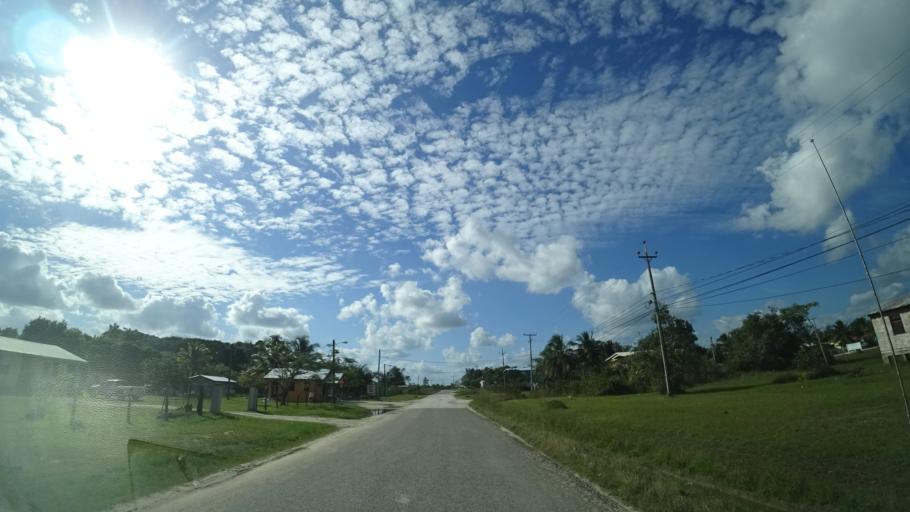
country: BZ
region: Belize
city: Belize City
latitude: 17.5695
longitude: -88.4175
